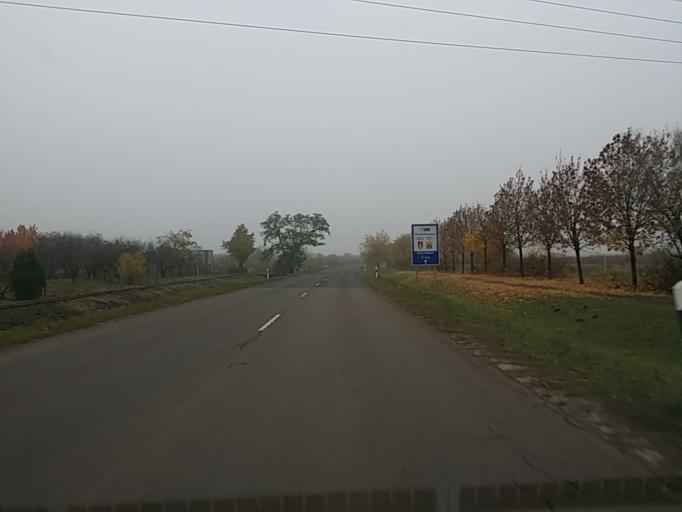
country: HU
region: Heves
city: Gyongyossolymos
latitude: 47.8030
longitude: 19.9485
